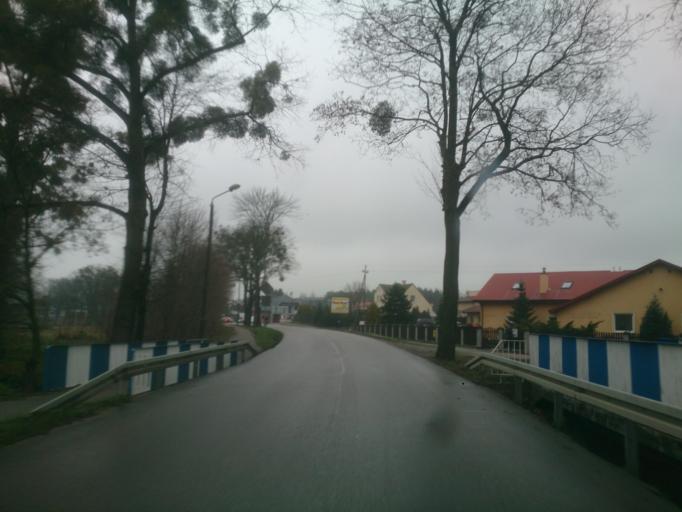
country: PL
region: Kujawsko-Pomorskie
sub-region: Powiat brodnicki
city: Brodnica
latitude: 53.2663
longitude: 19.3909
